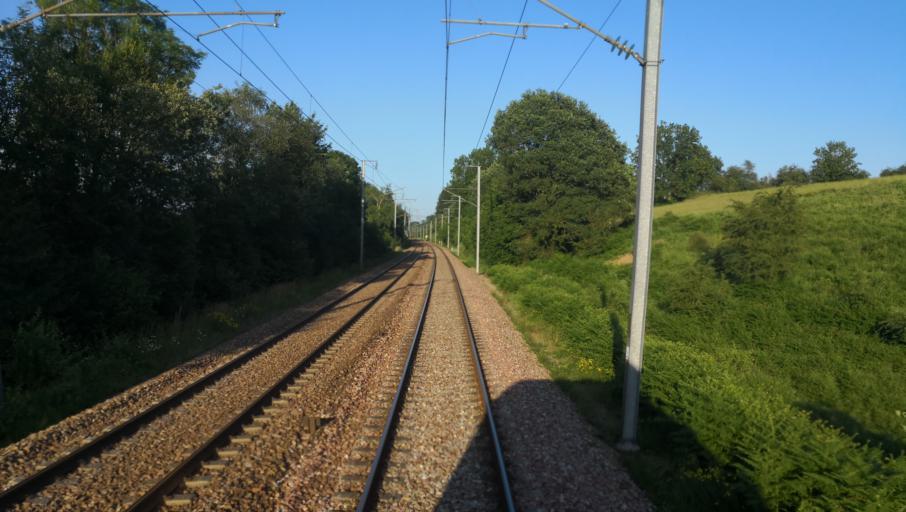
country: FR
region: Lower Normandy
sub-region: Departement du Calvados
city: Beuvillers
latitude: 49.1232
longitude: 0.3053
